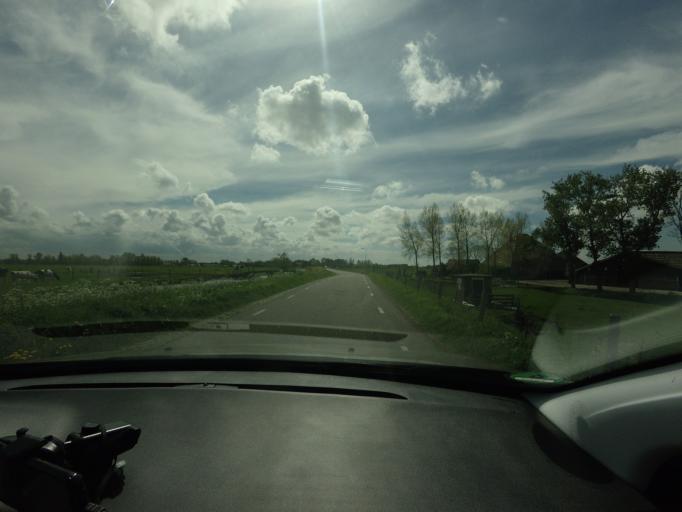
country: NL
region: North Holland
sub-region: Gemeente Beemster
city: Halfweg
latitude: 52.5682
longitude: 4.8341
